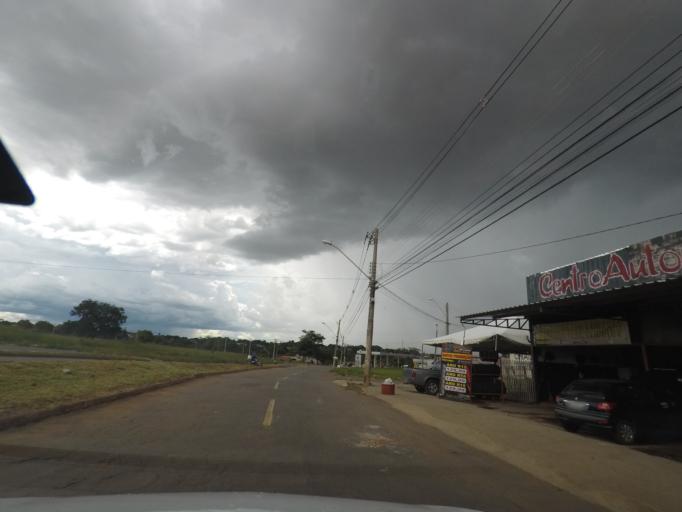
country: BR
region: Goias
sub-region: Goiania
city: Goiania
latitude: -16.7327
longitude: -49.3645
